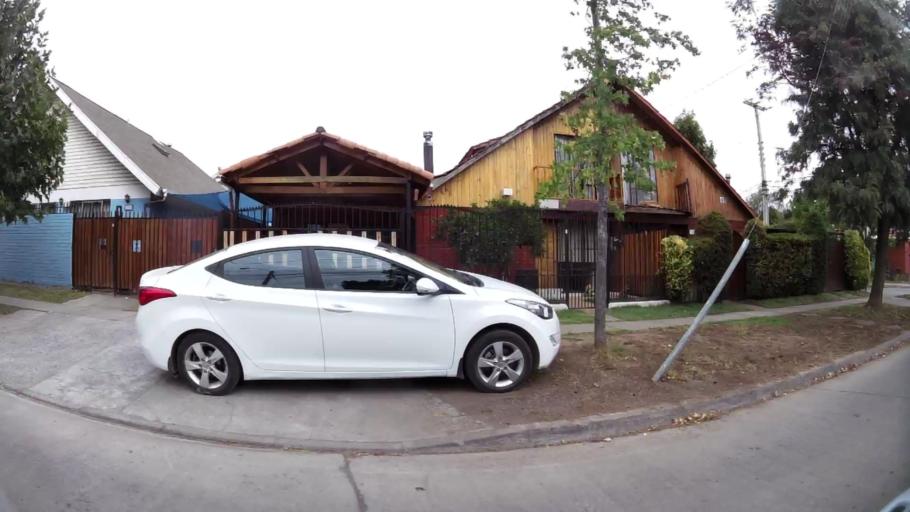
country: CL
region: O'Higgins
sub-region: Provincia de Cachapoal
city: Rancagua
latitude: -34.1399
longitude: -70.7316
